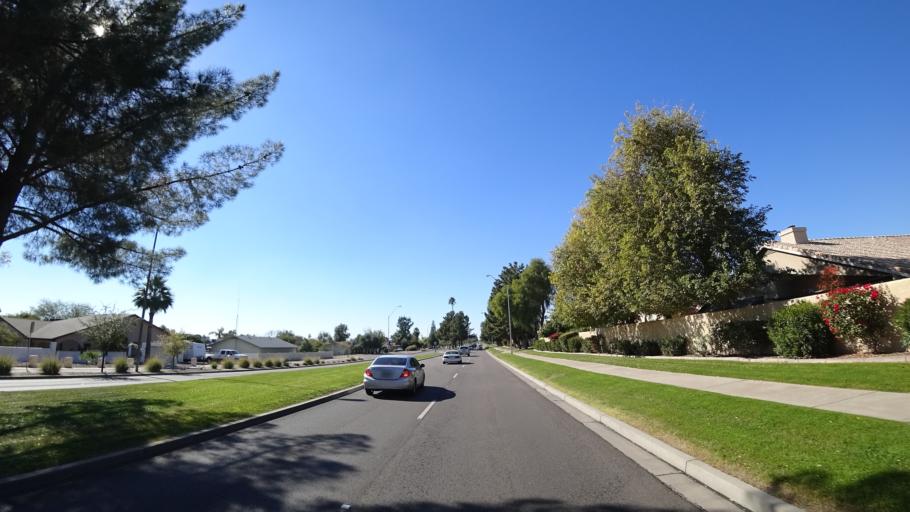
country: US
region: Arizona
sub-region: Maricopa County
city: Peoria
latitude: 33.6529
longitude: -112.2089
